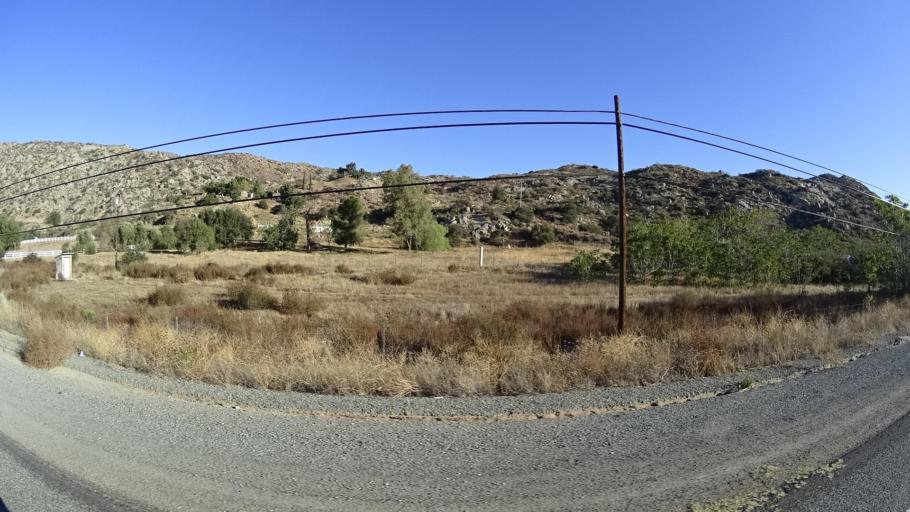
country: MX
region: Baja California
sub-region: Tecate
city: Hacienda Tecate
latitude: 32.5969
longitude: -116.5523
